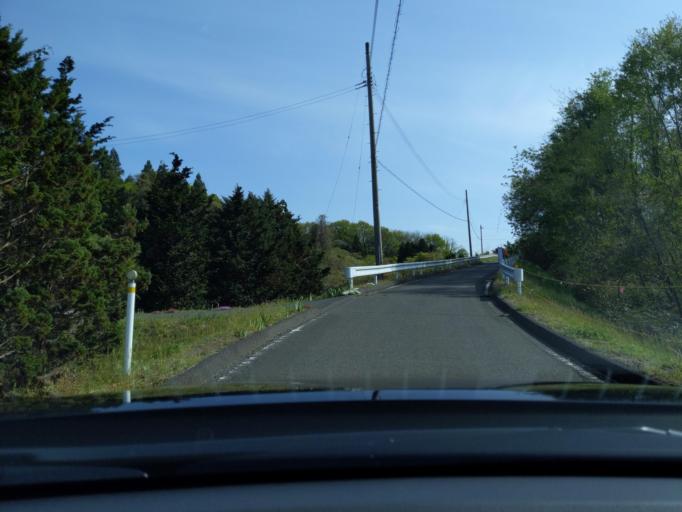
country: JP
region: Fukushima
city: Sukagawa
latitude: 37.3110
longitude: 140.4260
